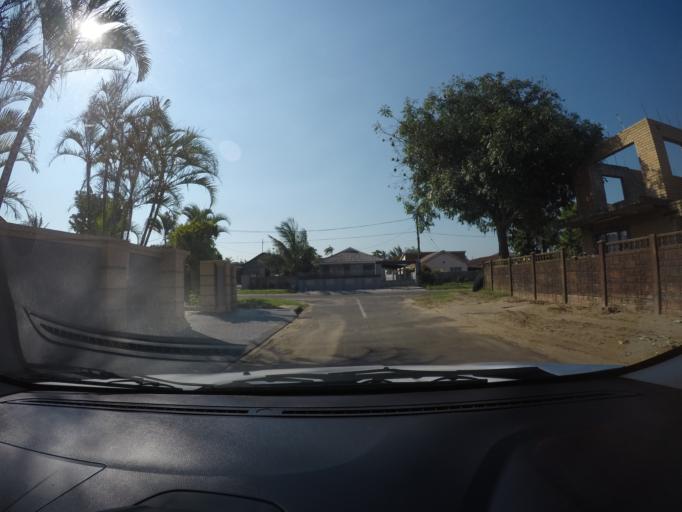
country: ZA
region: KwaZulu-Natal
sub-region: uThungulu District Municipality
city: Richards Bay
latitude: -28.7193
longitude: 32.0441
